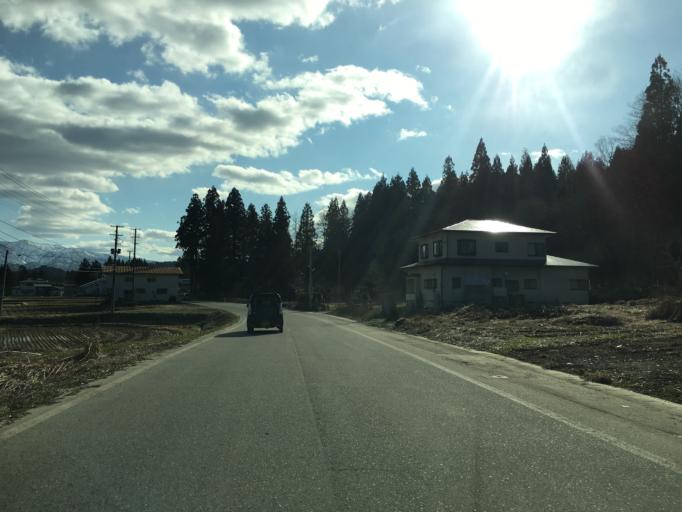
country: JP
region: Yamagata
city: Yonezawa
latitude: 37.9655
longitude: 139.9910
